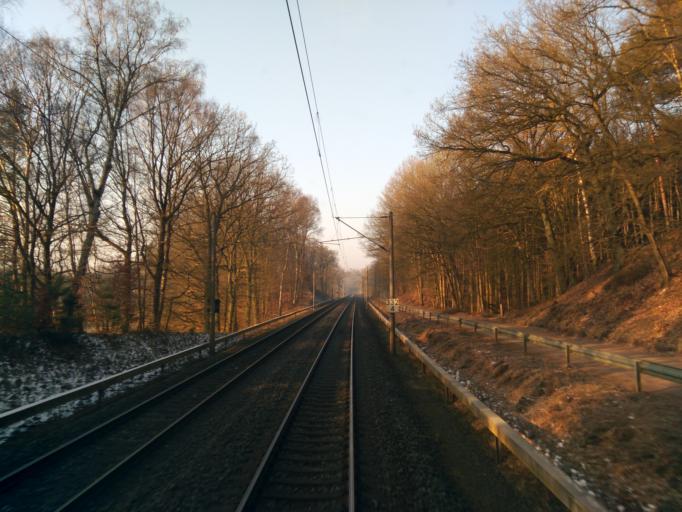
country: DE
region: Lower Saxony
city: Seevetal
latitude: 53.3895
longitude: 9.9555
